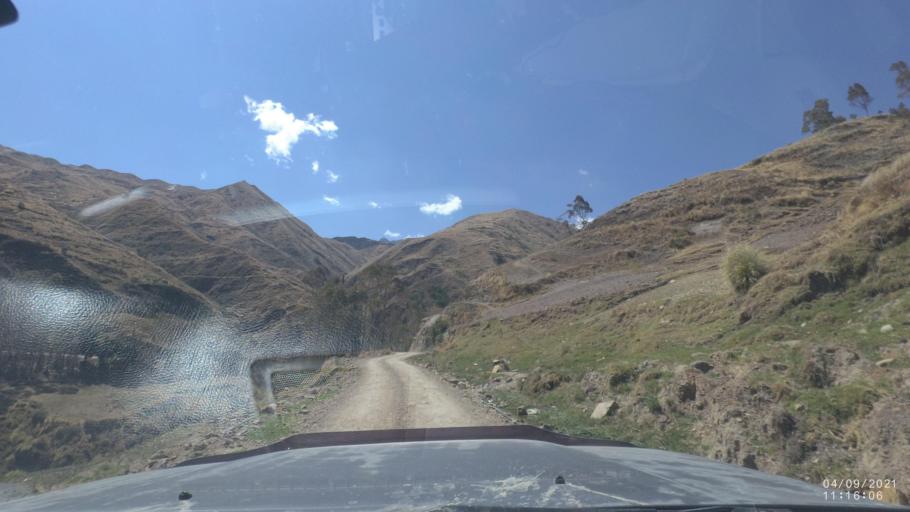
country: BO
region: Cochabamba
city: Sipe Sipe
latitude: -17.2716
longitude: -66.4868
